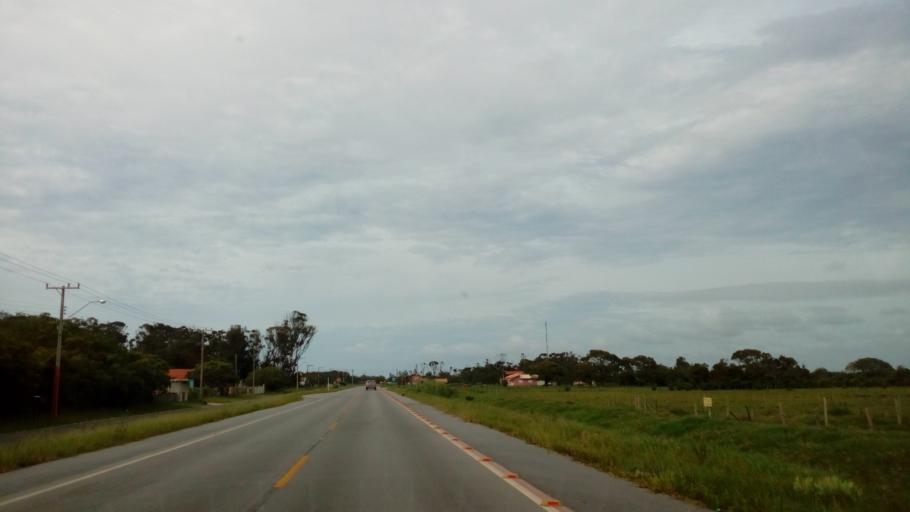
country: BR
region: Santa Catarina
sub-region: Laguna
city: Laguna
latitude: -28.5467
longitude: -48.7939
